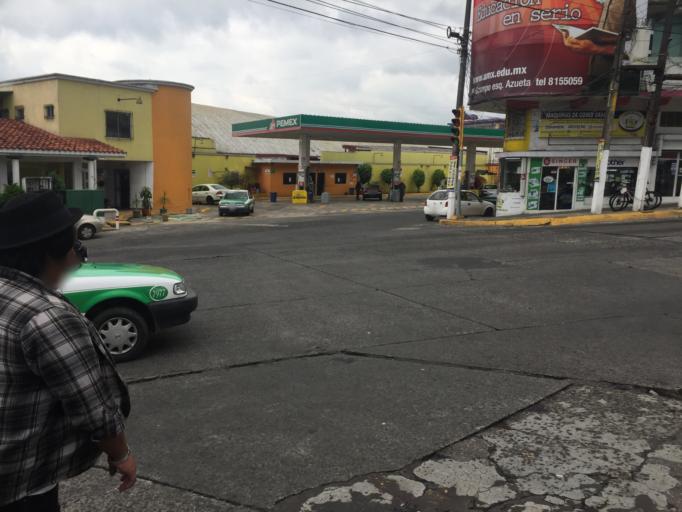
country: MX
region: Veracruz
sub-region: Xalapa
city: Xalapa de Enriquez
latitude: 19.5372
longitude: -96.9235
